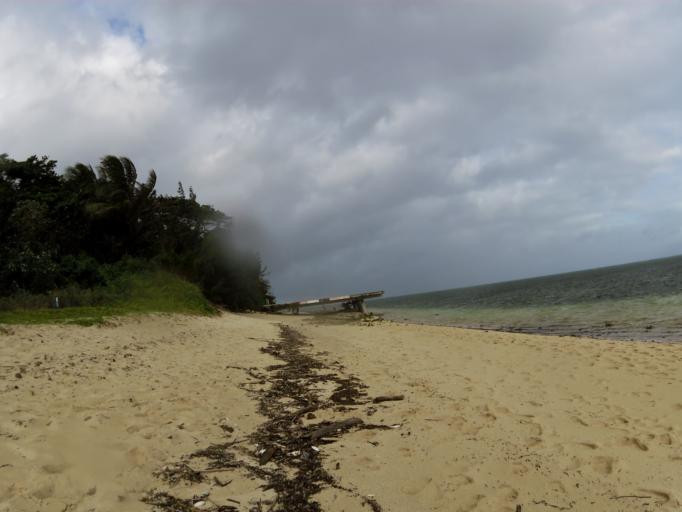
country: AU
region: Queensland
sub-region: Cairns
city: Yorkeys Knob
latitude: -16.7600
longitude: 145.9714
